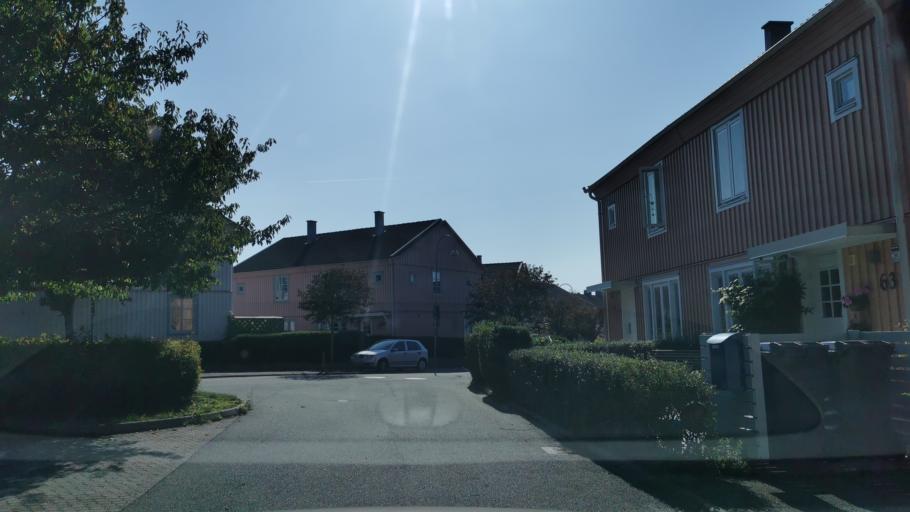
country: SE
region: Vaestra Goetaland
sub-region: Goteborg
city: Goeteborg
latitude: 57.6565
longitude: 11.9598
